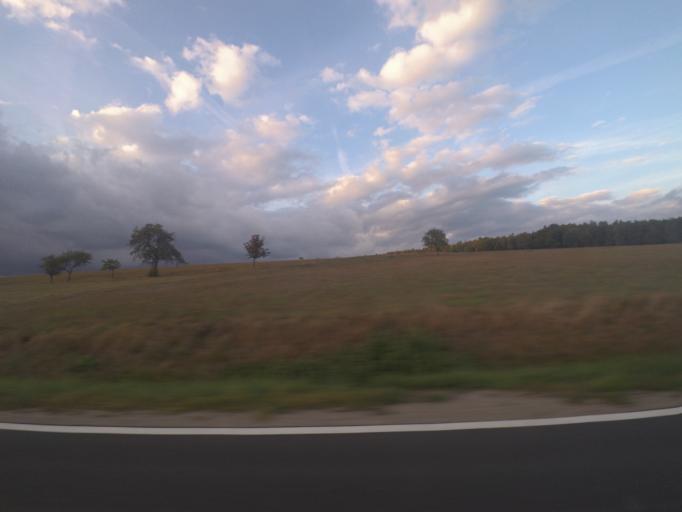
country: DE
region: Bavaria
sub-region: Regierungsbezirk Unterfranken
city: Schondra
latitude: 50.2491
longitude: 9.8908
